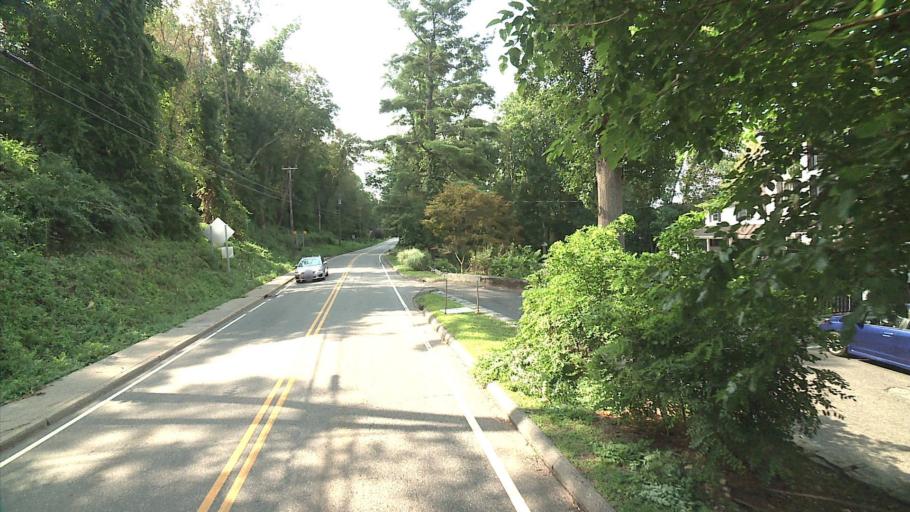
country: US
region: Connecticut
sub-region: Middlesex County
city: East Haddam
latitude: 41.4619
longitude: -72.4641
